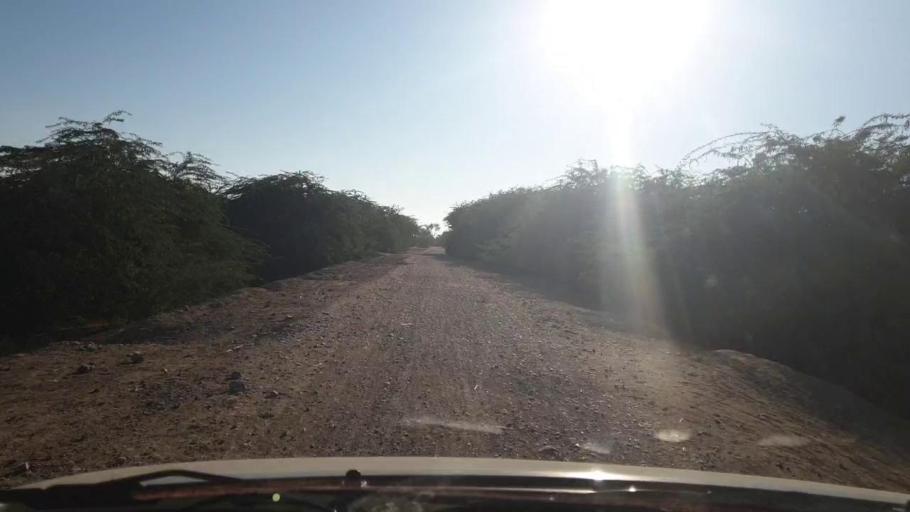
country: PK
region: Sindh
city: Johi
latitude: 26.7506
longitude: 67.4812
